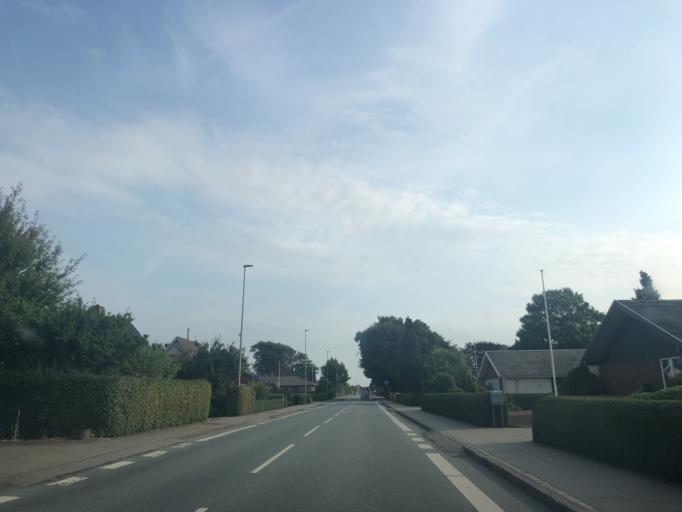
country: DK
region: Central Jutland
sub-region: Holstebro Kommune
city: Vinderup
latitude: 56.6192
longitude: 8.8800
